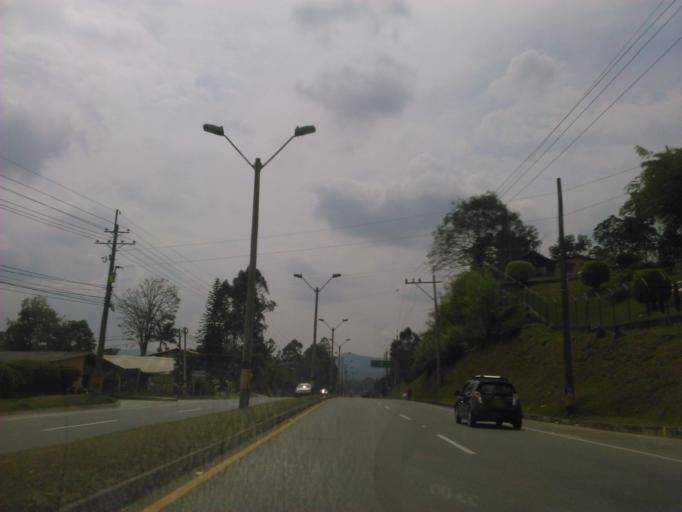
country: CO
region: Antioquia
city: San Vicente
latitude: 6.2285
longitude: -75.4005
